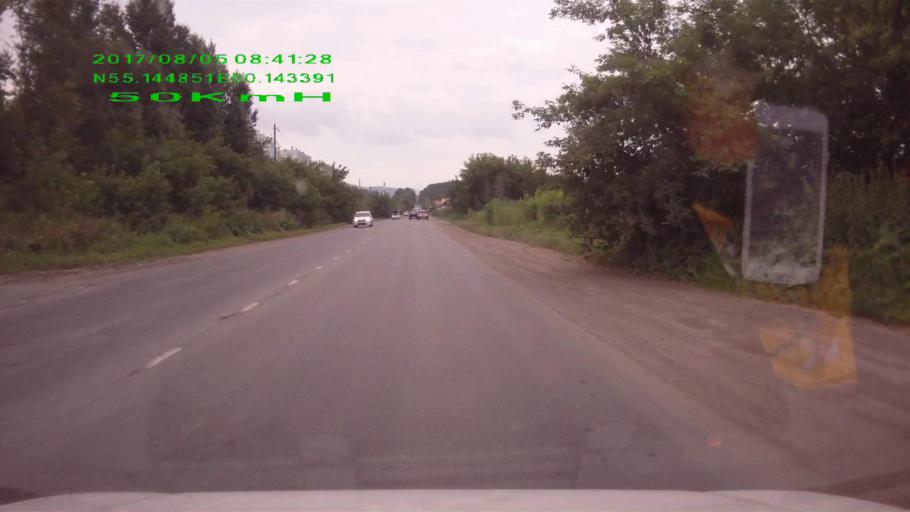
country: RU
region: Chelyabinsk
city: Turgoyak
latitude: 55.1446
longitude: 60.1434
